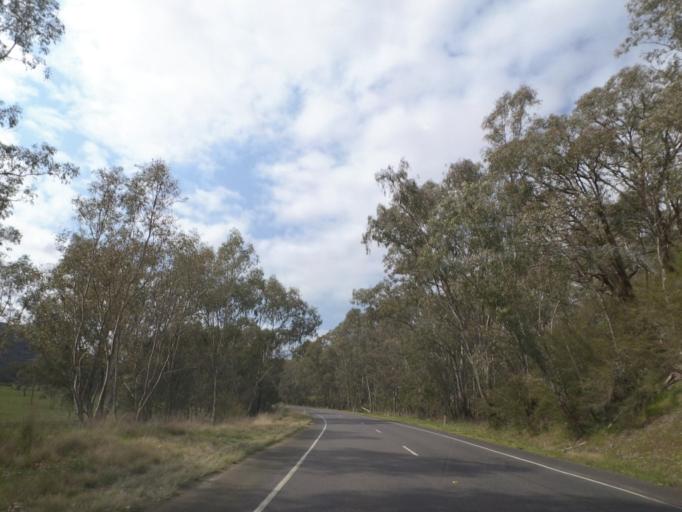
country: AU
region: Victoria
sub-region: Murrindindi
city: Kinglake West
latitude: -37.1435
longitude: 145.2544
